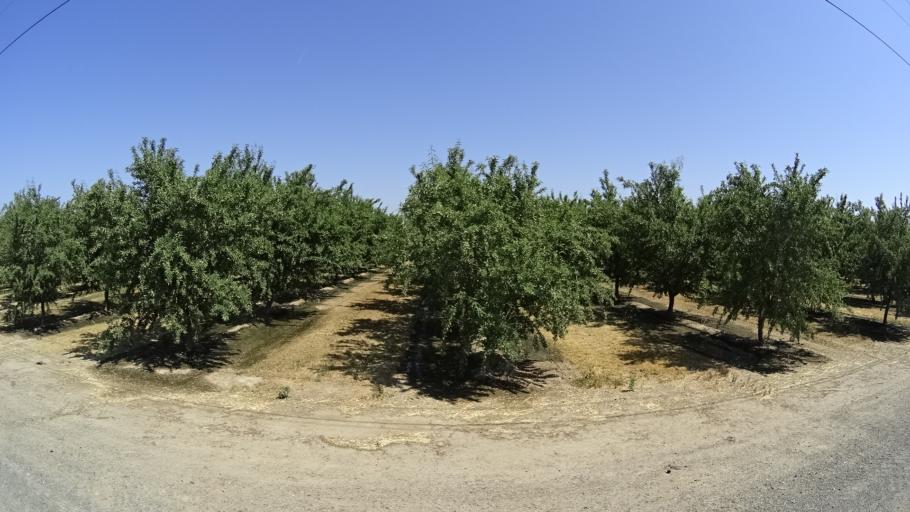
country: US
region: California
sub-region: Kings County
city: Hanford
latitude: 36.3716
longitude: -119.6024
